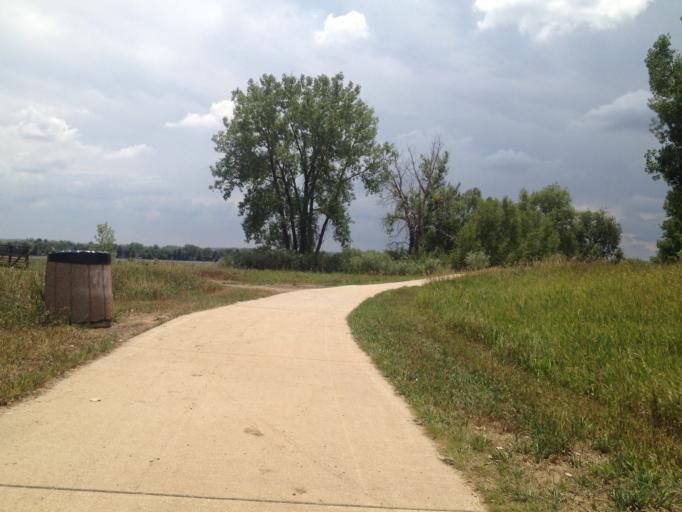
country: US
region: Colorado
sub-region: Boulder County
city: Louisville
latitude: 39.9703
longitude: -105.1469
